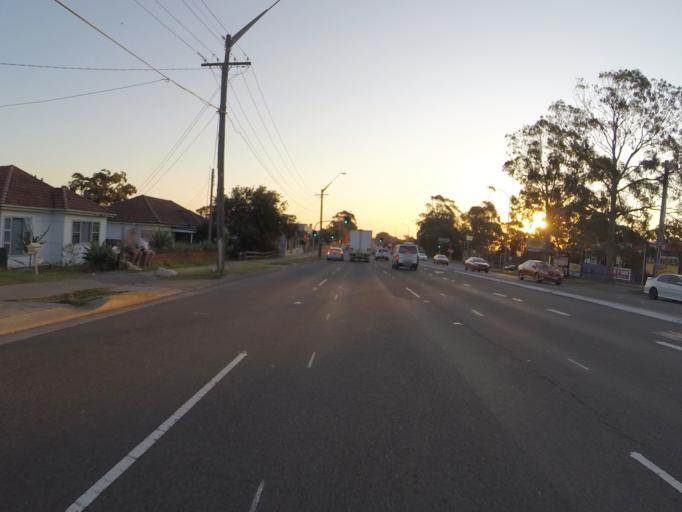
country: AU
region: New South Wales
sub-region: Hurstville
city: Peakhurst
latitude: -33.9586
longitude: 151.0647
